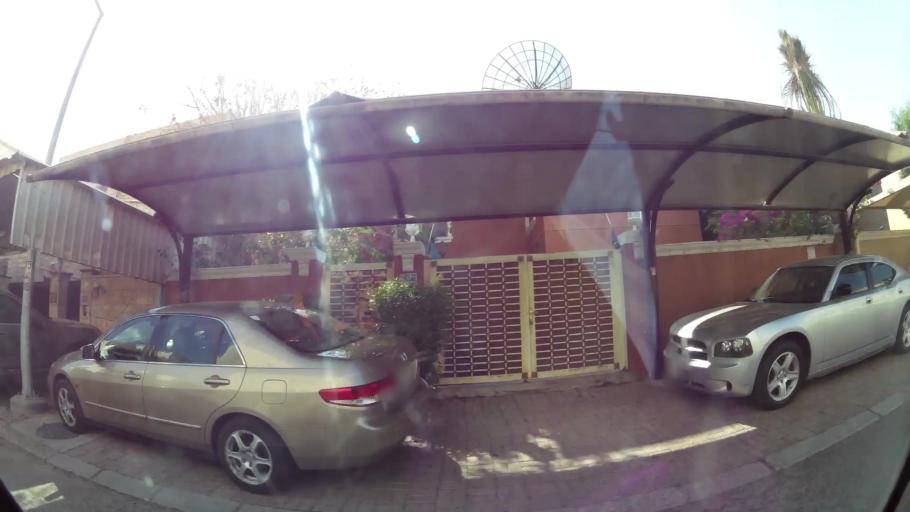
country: KW
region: Muhafazat Hawalli
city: Salwa
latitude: 29.2816
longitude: 48.0797
